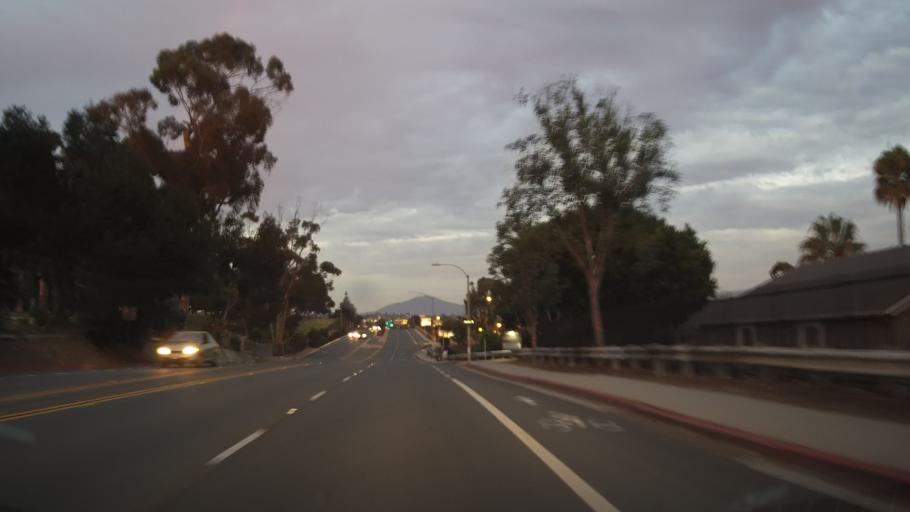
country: US
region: California
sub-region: San Diego County
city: National City
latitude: 32.7042
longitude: -117.1062
